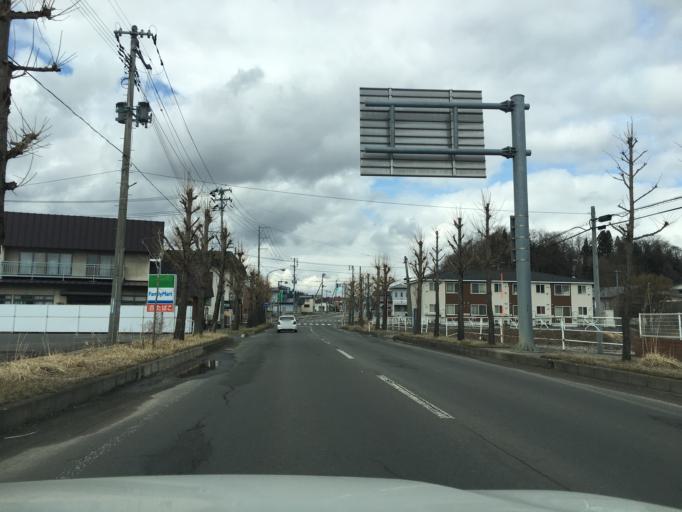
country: JP
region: Akita
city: Hanawa
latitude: 40.2666
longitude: 140.7696
